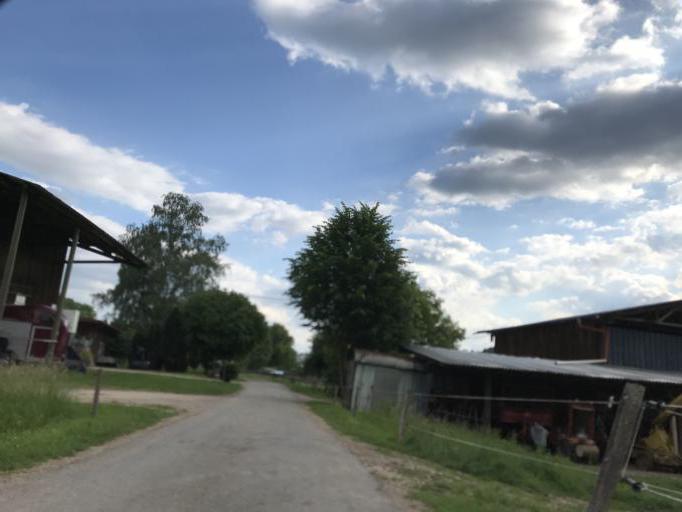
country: DE
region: Baden-Wuerttemberg
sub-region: Freiburg Region
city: Hausen
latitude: 47.6662
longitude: 7.8412
